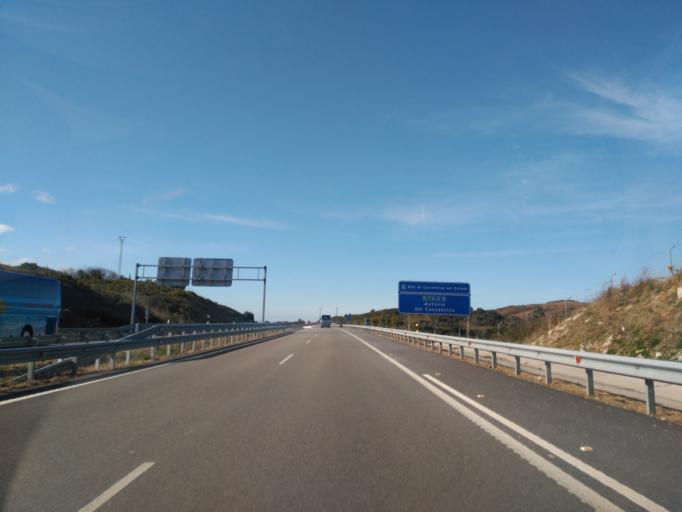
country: ES
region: Asturias
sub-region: Province of Asturias
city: Llanes
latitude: 43.3982
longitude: -4.6586
